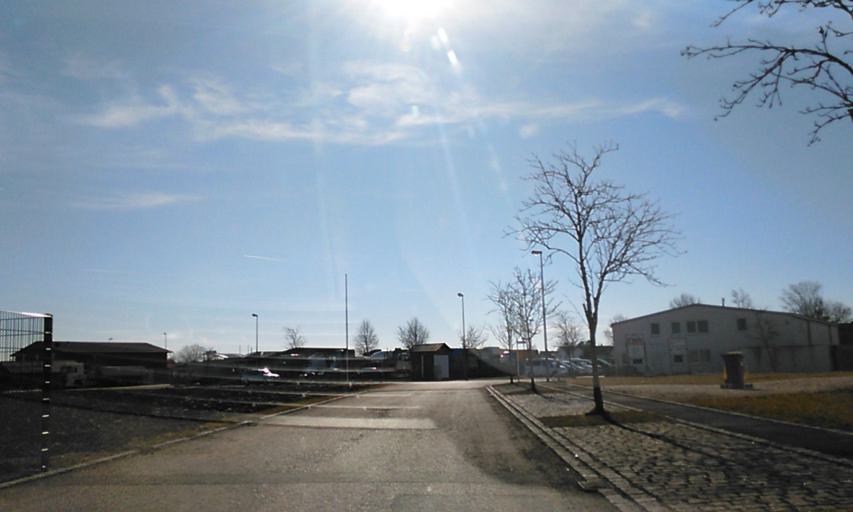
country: DE
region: Bavaria
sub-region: Swabia
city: Merching
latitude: 48.2465
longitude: 10.9944
